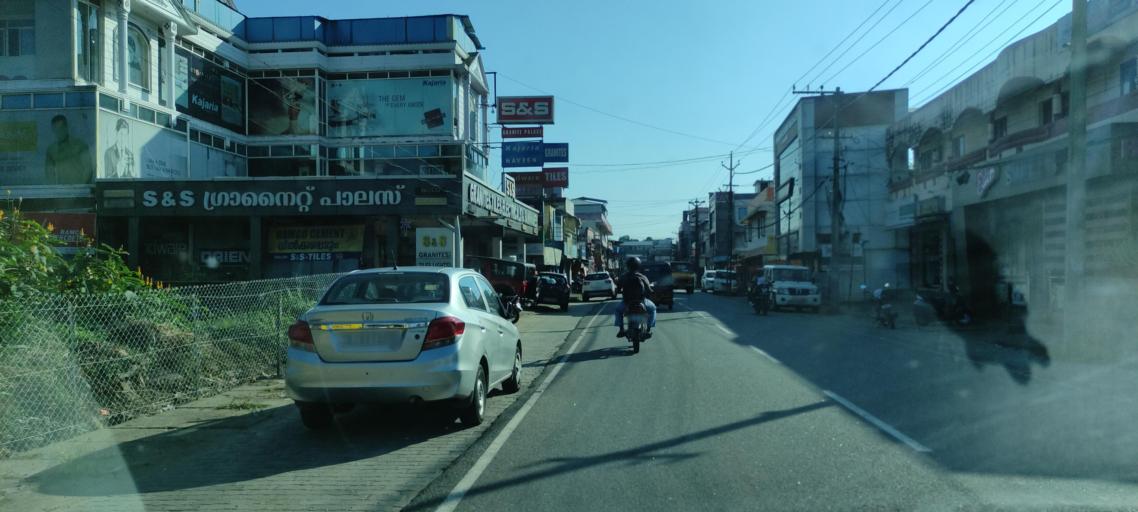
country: IN
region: Kerala
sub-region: Pattanamtitta
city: Pathanamthitta
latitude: 9.2419
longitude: 76.7559
